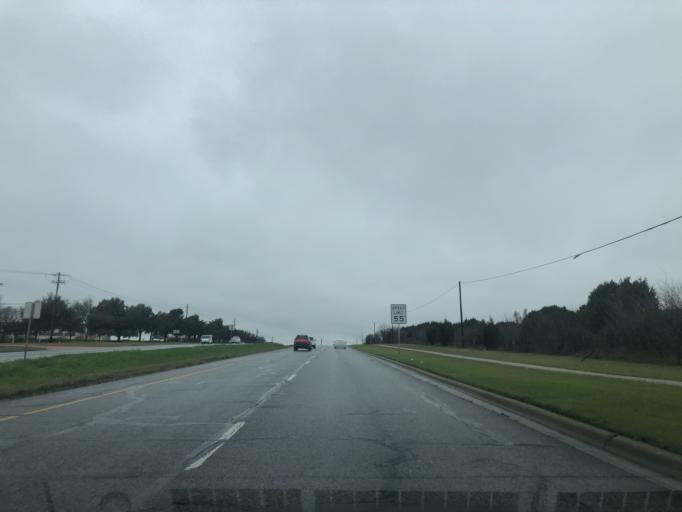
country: US
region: Texas
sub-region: Travis County
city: Wells Branch
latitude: 30.4026
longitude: -97.6573
